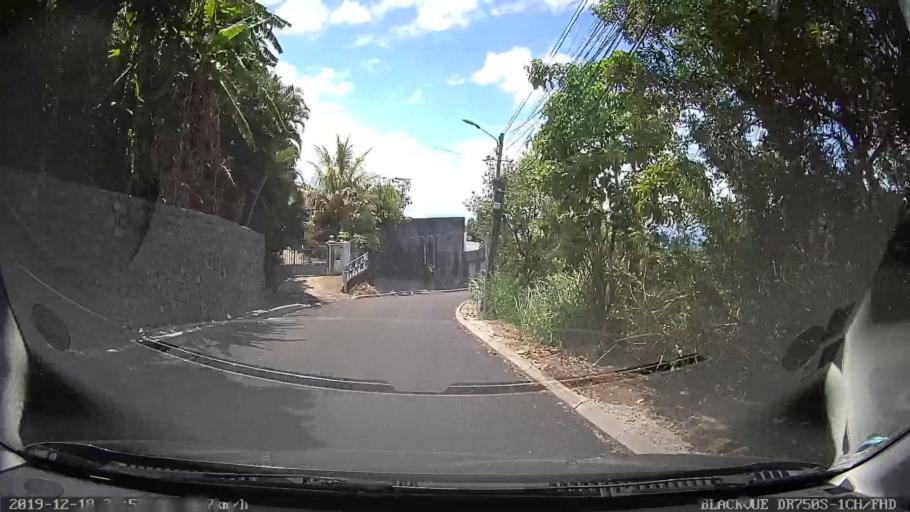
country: RE
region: Reunion
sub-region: Reunion
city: Sainte-Marie
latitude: -20.9423
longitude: 55.5296
